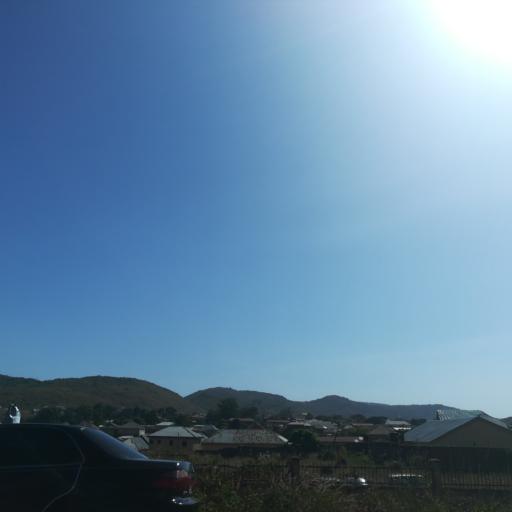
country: NG
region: Plateau
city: Jos
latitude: 9.9376
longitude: 8.9075
